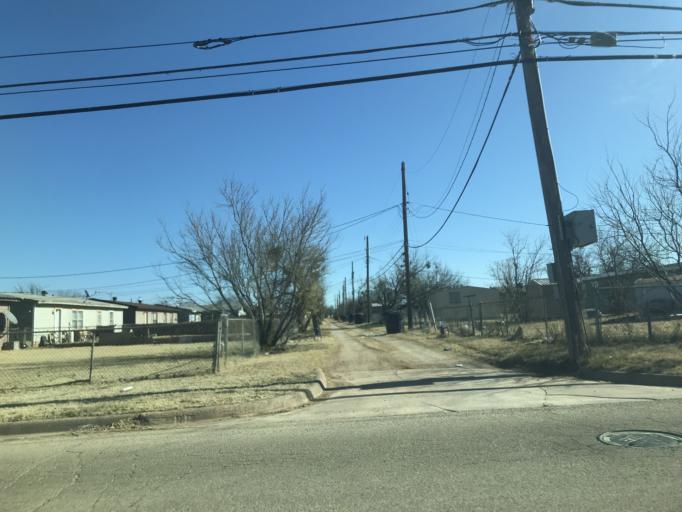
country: US
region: Texas
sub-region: Taylor County
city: Abilene
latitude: 32.4437
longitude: -99.7945
